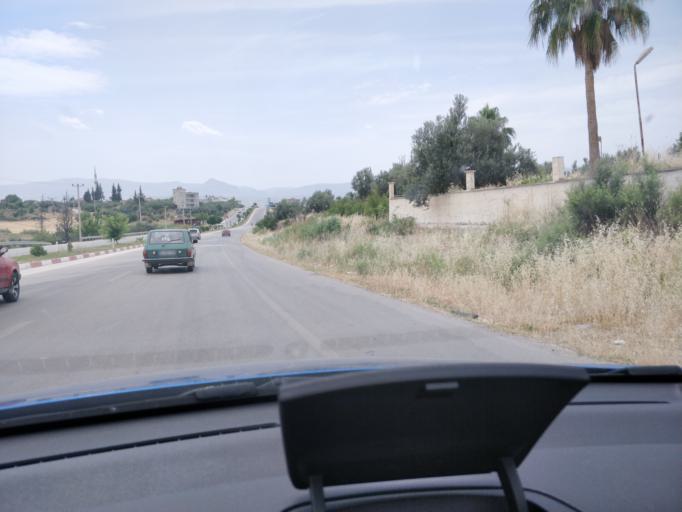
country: TR
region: Mersin
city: Mut
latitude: 36.6143
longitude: 33.4409
